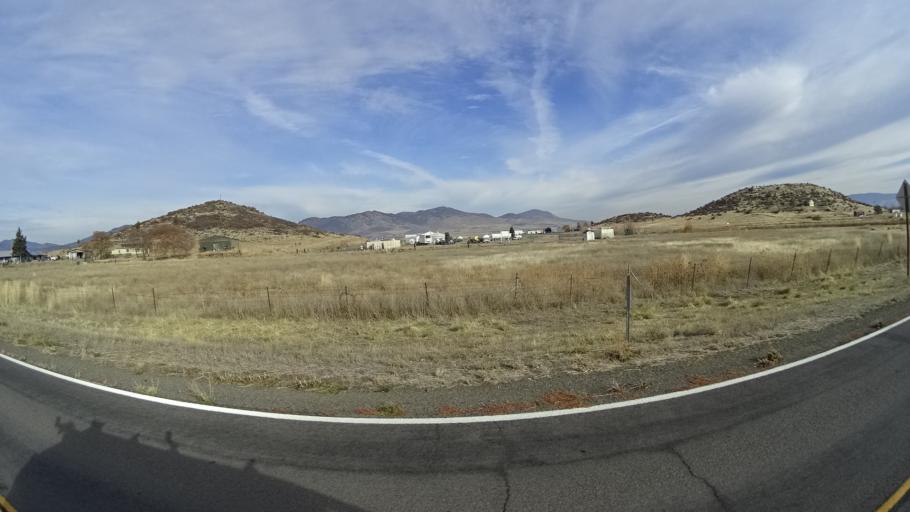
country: US
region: California
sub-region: Siskiyou County
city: Montague
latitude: 41.7247
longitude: -122.5447
